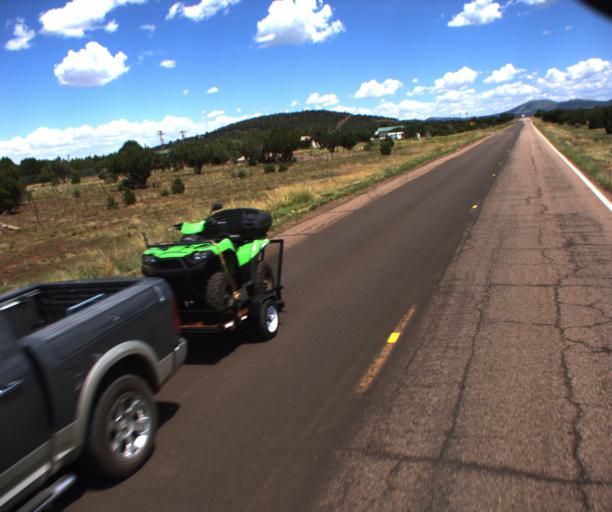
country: US
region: Arizona
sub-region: Navajo County
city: Pinetop-Lakeside
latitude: 34.2720
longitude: -109.7489
